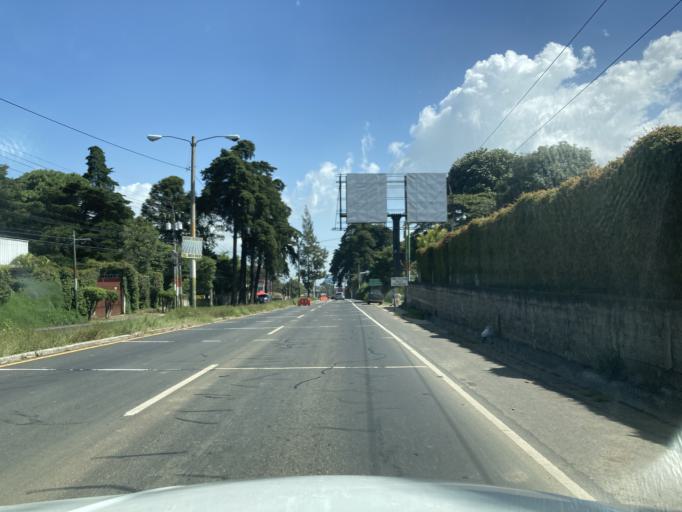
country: GT
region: Guatemala
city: Fraijanes
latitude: 14.4719
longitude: -90.4853
